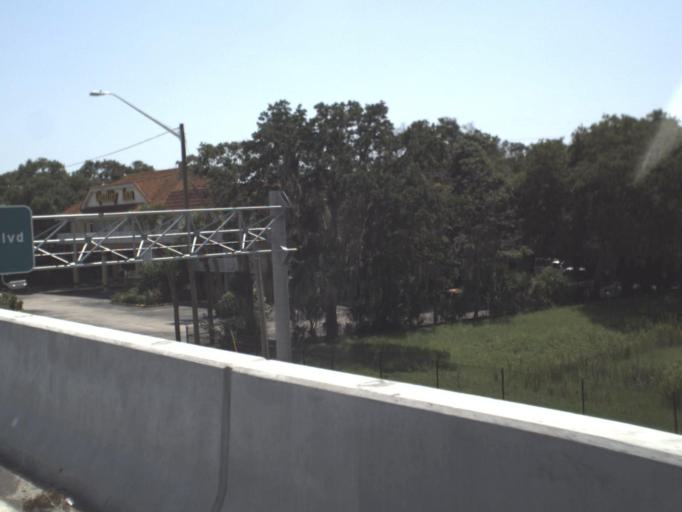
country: US
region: Florida
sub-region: Pinellas County
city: South Highpoint
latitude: 27.9565
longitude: -82.7303
